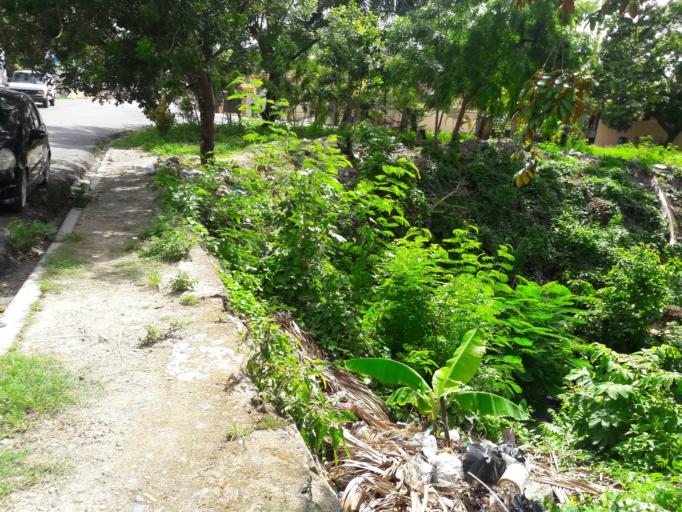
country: DO
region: Nacional
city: Ensanche Luperon
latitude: 18.5224
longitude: -69.9137
